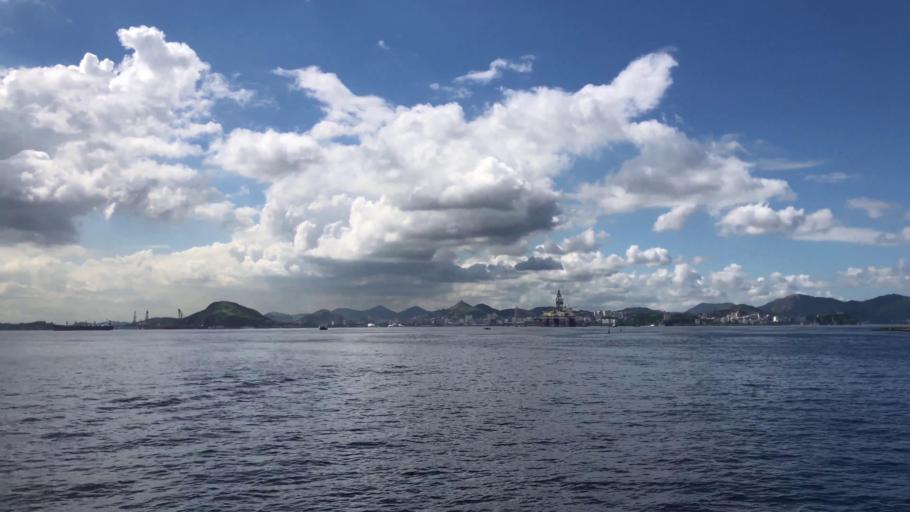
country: BR
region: Rio de Janeiro
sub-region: Rio De Janeiro
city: Rio de Janeiro
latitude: -22.9012
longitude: -43.1648
